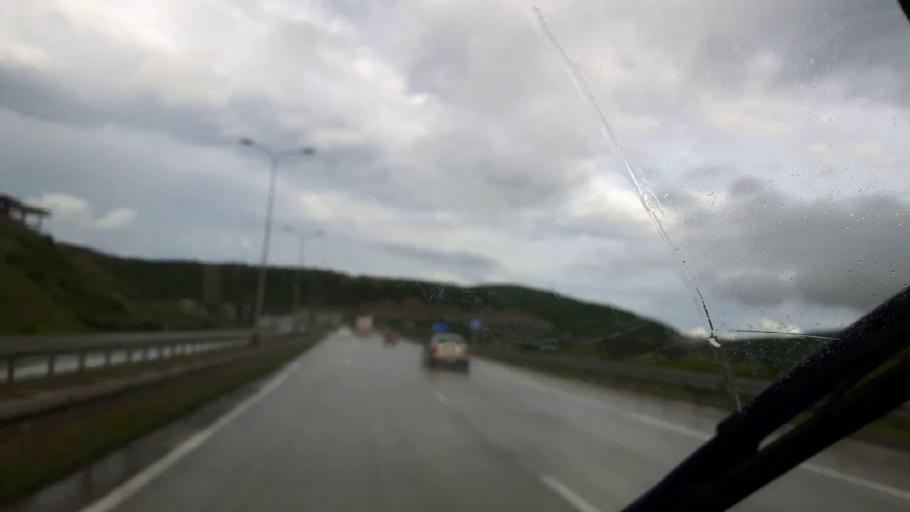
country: GE
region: Shida Kartli
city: Kaspi
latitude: 41.9957
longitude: 44.4129
